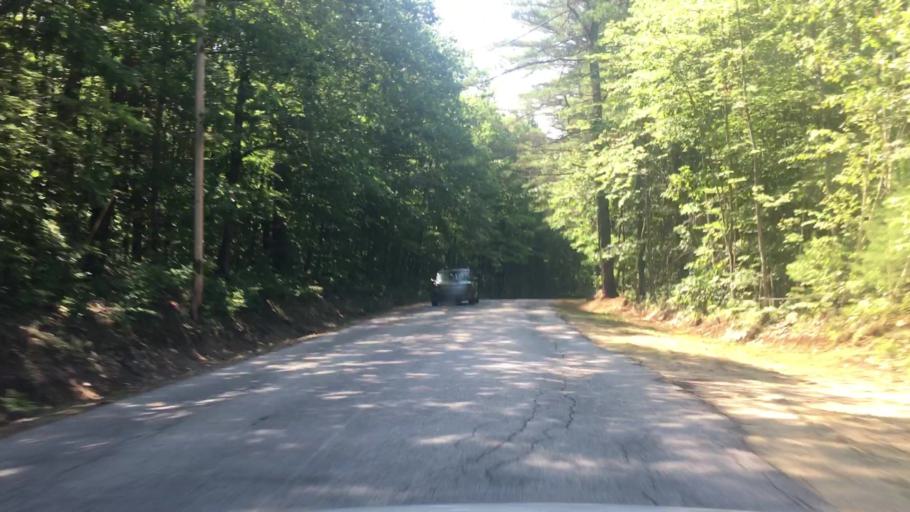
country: US
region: Maine
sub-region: Oxford County
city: South Paris
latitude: 44.2088
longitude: -70.5130
